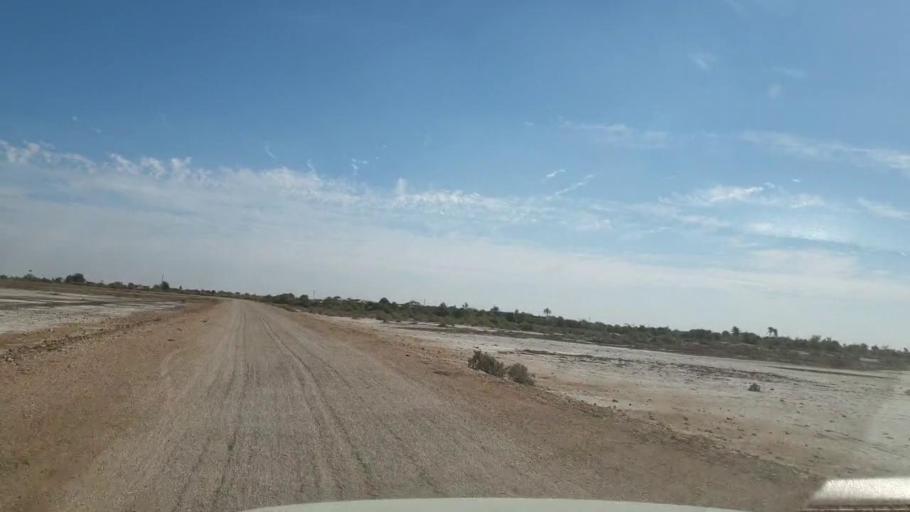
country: PK
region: Sindh
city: Pithoro
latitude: 25.5825
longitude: 69.2884
